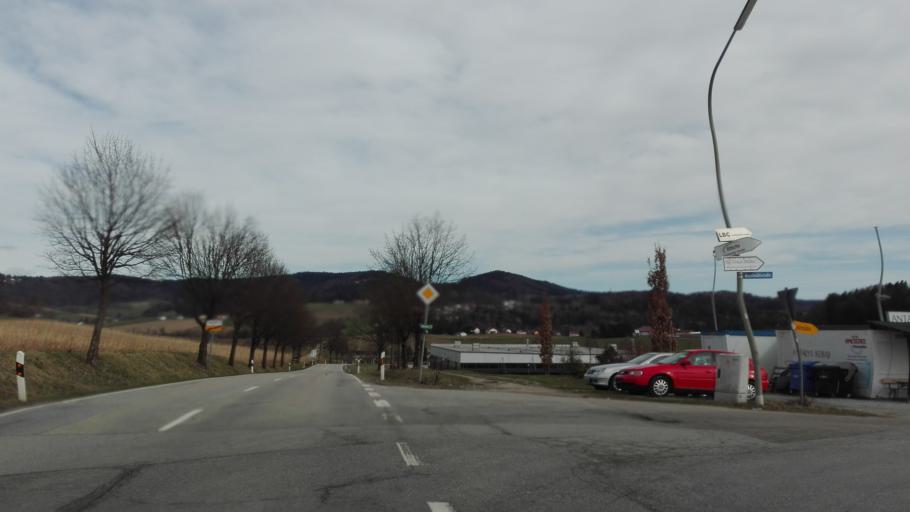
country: DE
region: Bavaria
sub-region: Lower Bavaria
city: Hauzenberg
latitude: 48.6295
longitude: 13.6437
